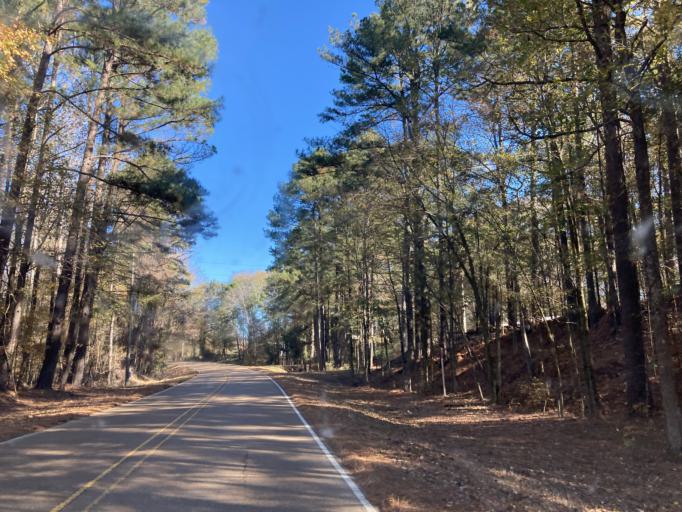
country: US
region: Mississippi
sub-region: Hinds County
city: Lynchburg
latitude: 32.6228
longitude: -90.5234
